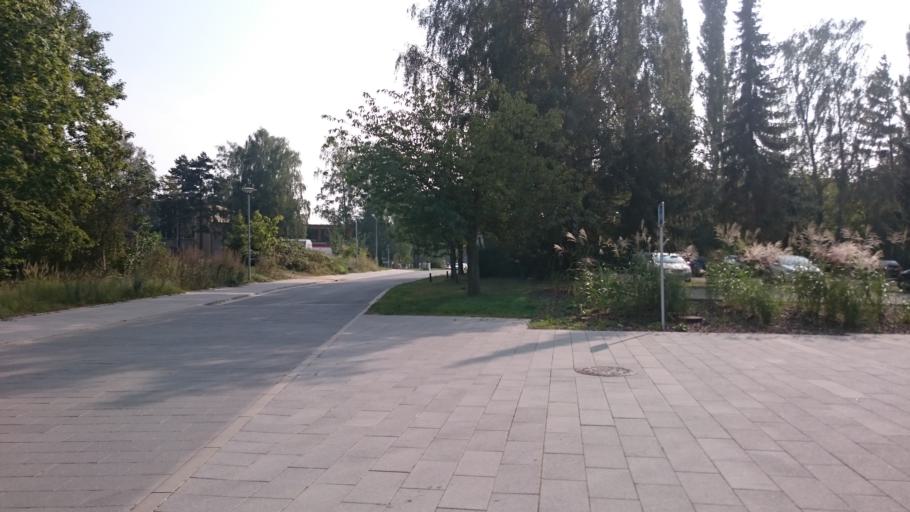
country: DE
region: Mecklenburg-Vorpommern
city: Rostock
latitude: 54.0785
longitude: 12.1125
